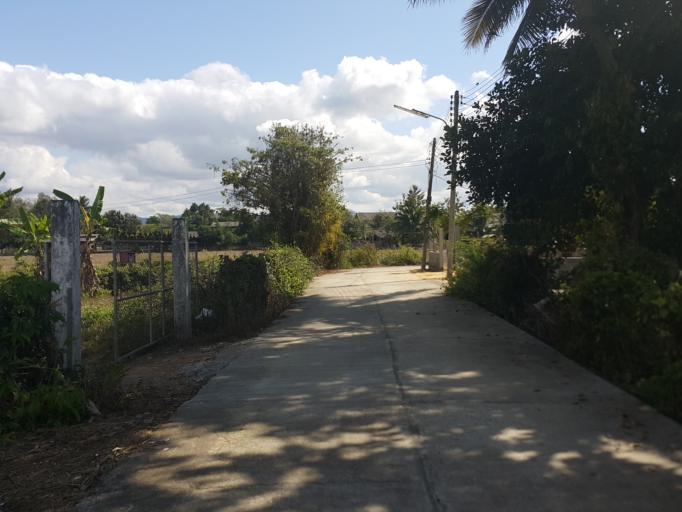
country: TH
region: Chiang Mai
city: San Kamphaeng
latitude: 18.7993
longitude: 99.1379
